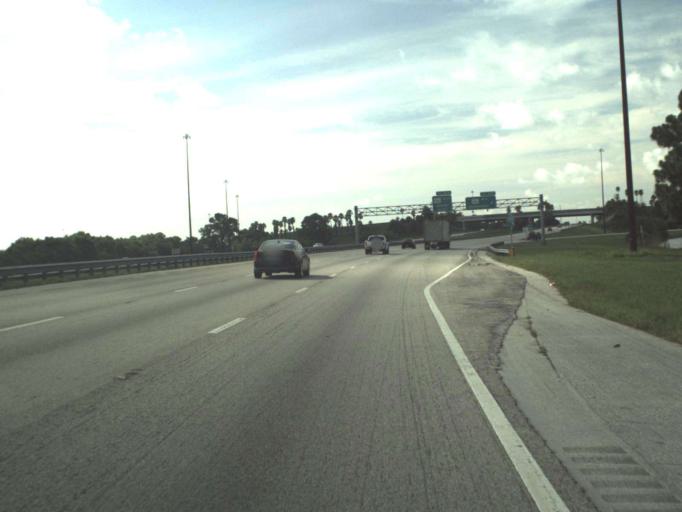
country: US
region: Florida
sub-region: Palm Beach County
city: Limestone Creek
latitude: 26.9415
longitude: -80.1527
